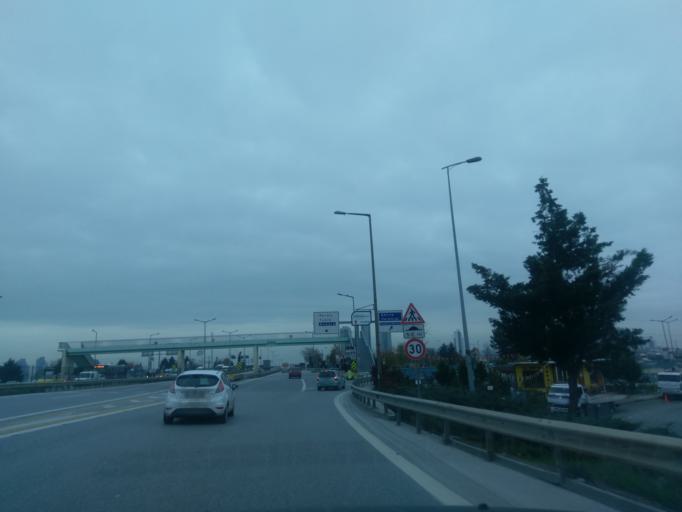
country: TR
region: Istanbul
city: Maltepe
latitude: 40.9079
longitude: 29.2124
